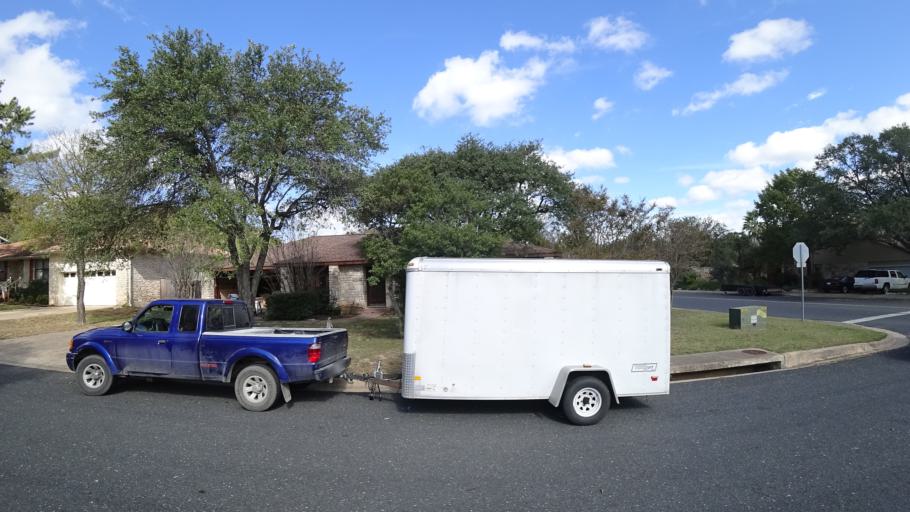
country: US
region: Texas
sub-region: Williamson County
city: Anderson Mill
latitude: 30.4253
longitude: -97.8020
